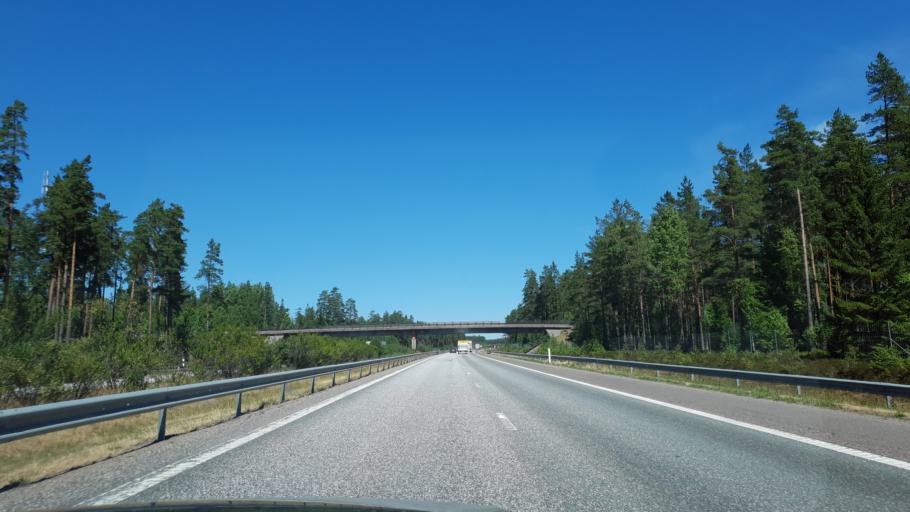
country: SE
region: Joenkoeping
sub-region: Vaggeryds Kommun
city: Vaggeryd
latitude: 57.5478
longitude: 14.1309
